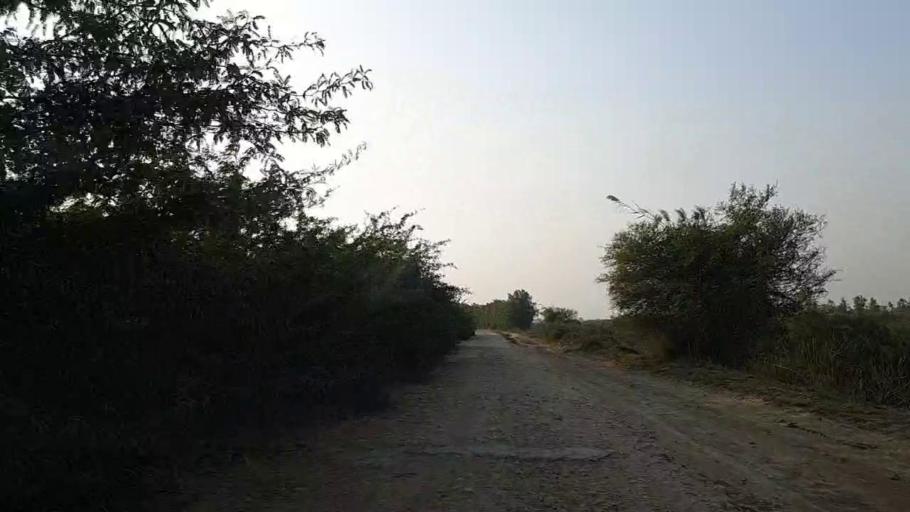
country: PK
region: Sindh
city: Thatta
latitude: 24.6922
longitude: 67.7901
